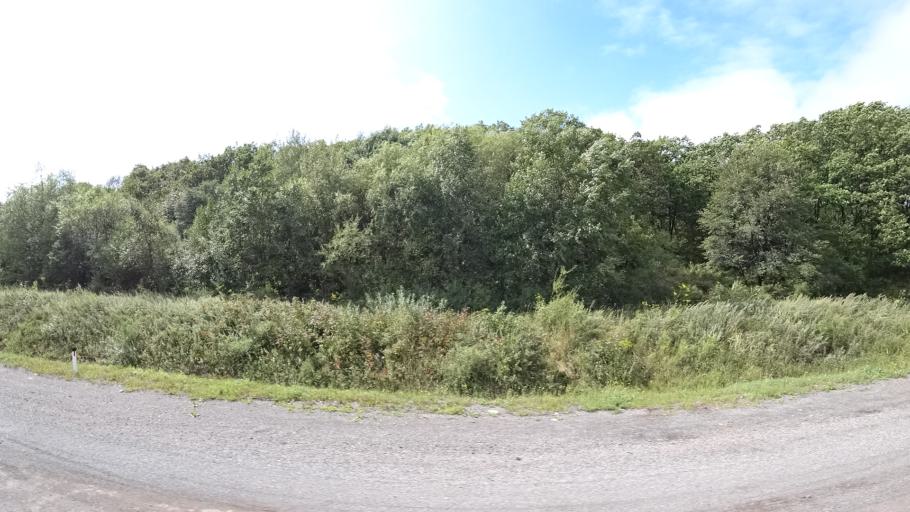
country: RU
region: Primorskiy
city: Lyalichi
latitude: 44.1319
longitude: 132.4273
